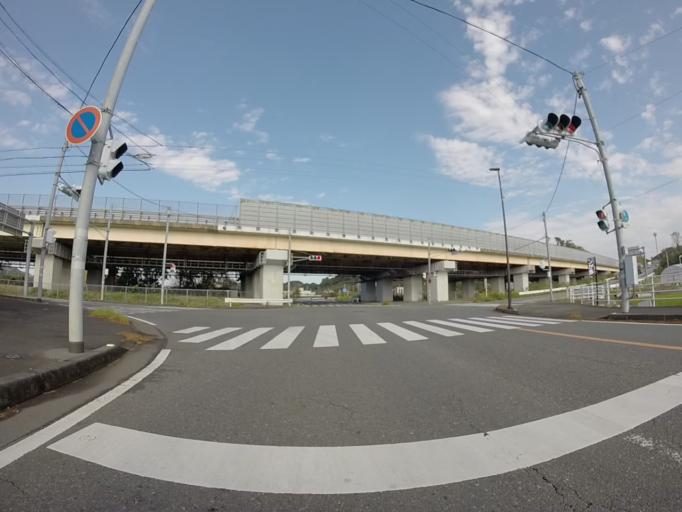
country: JP
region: Shizuoka
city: Shimada
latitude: 34.7750
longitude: 138.2286
